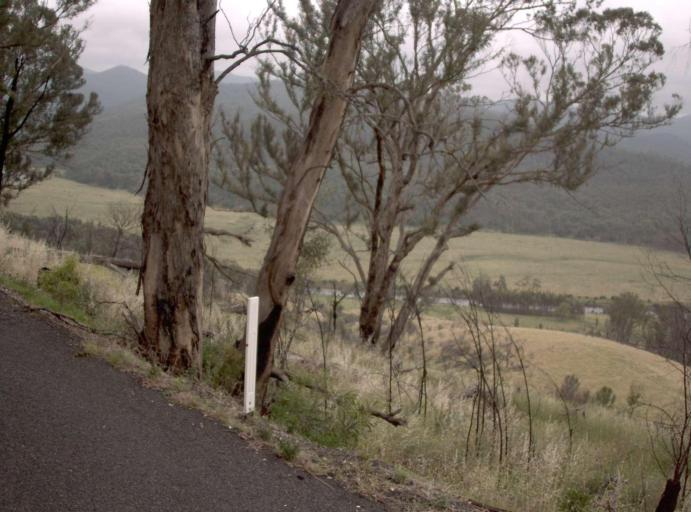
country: AU
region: Victoria
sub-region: Wellington
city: Heyfield
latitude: -37.8219
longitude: 146.6754
